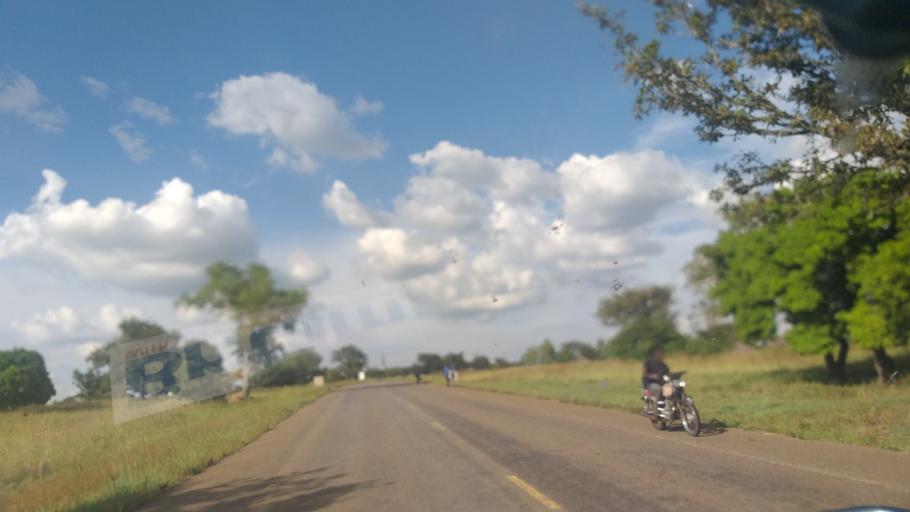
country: UG
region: Northern Region
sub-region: Nebbi District
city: Nebbi
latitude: 2.5316
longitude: 31.0920
